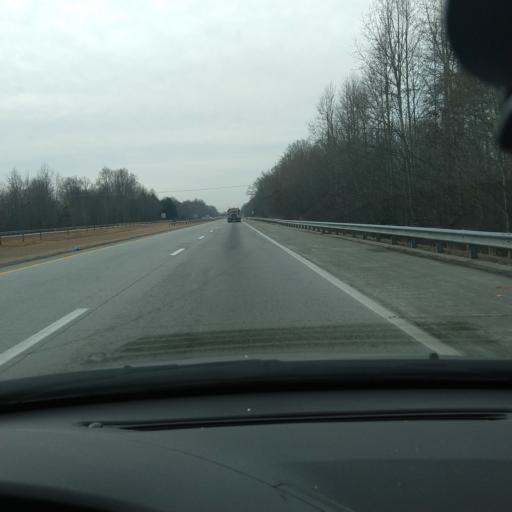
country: US
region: North Carolina
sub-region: Davidson County
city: Lexington
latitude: 35.8295
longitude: -80.2836
